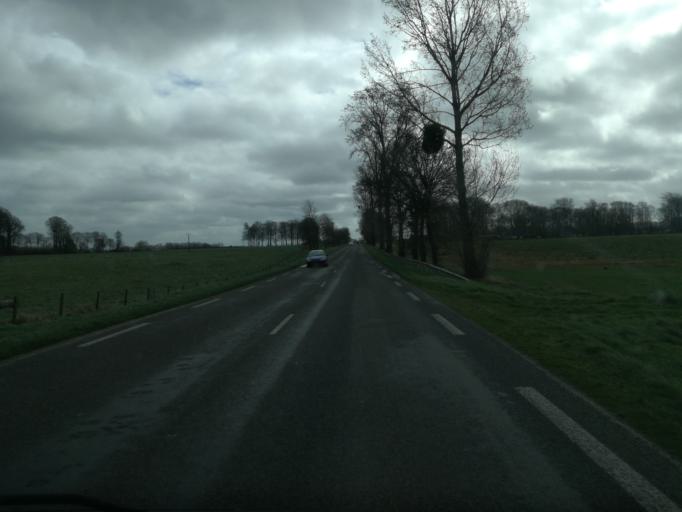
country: FR
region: Haute-Normandie
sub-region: Departement de la Seine-Maritime
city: Valliquerville
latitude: 49.6213
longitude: 0.6523
